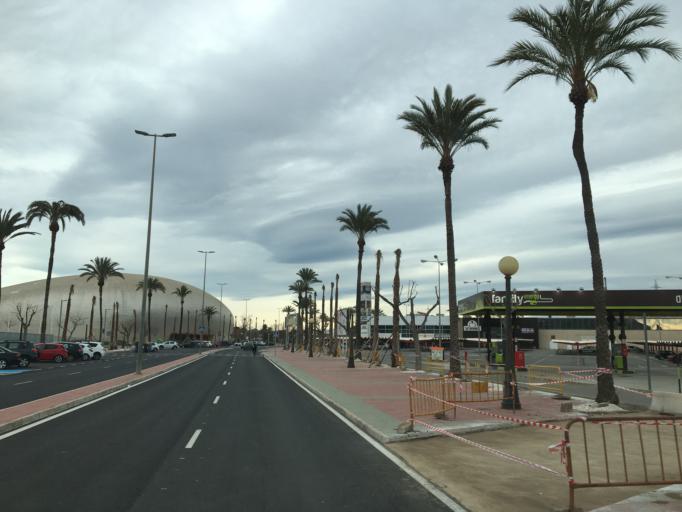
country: ES
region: Murcia
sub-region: Murcia
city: Cartagena
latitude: 37.6120
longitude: -1.0047
